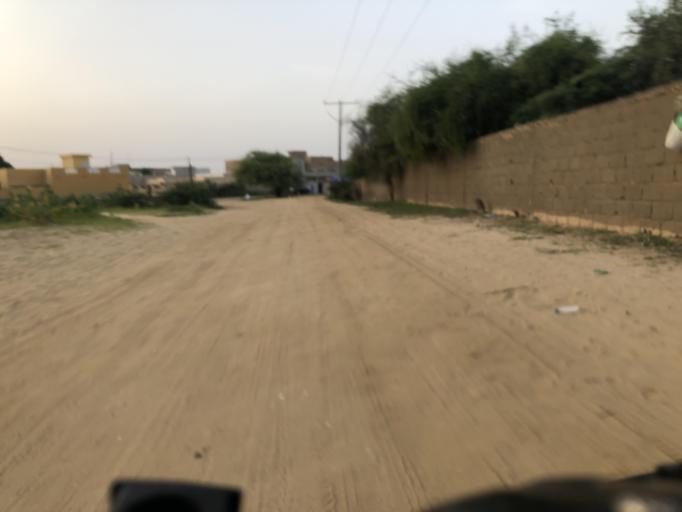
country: SN
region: Saint-Louis
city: Saint-Louis
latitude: 16.0504
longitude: -16.4338
